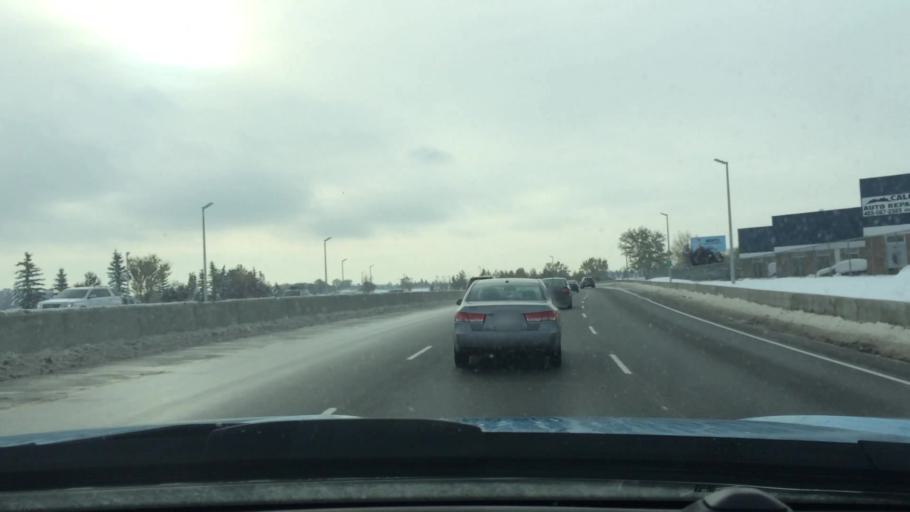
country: CA
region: Alberta
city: Calgary
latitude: 51.0949
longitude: -114.0273
